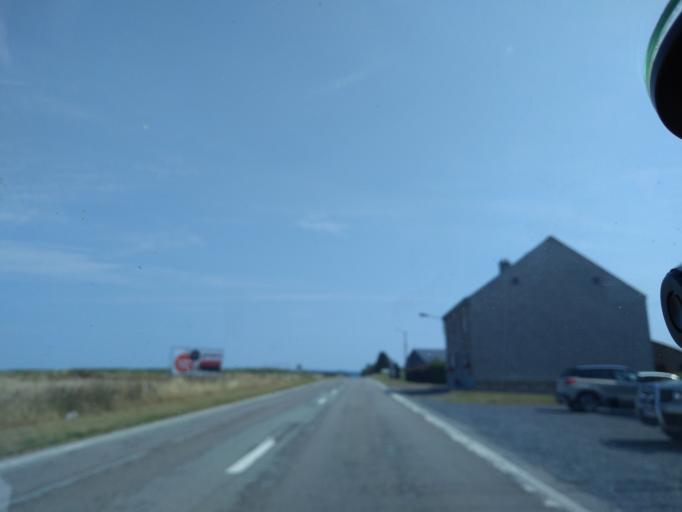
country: BE
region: Wallonia
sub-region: Province du Luxembourg
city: La Roche-en-Ardenne
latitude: 50.1548
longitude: 5.5243
